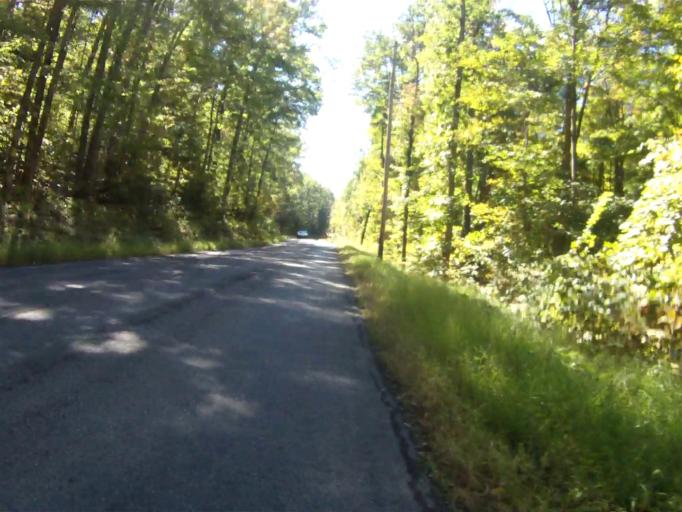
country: US
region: Pennsylvania
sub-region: Centre County
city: Houserville
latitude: 40.8906
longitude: -77.8815
